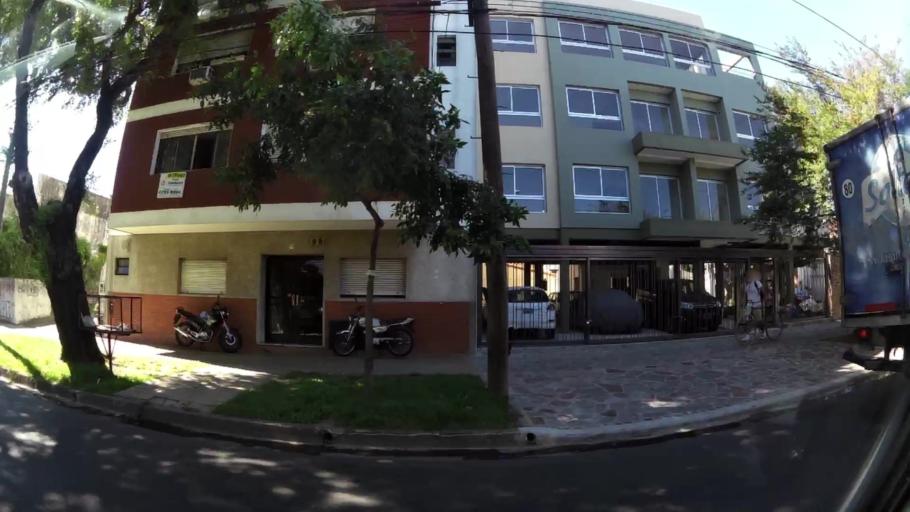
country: AR
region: Buenos Aires
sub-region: Partido de Vicente Lopez
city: Olivos
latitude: -34.5264
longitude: -58.4965
